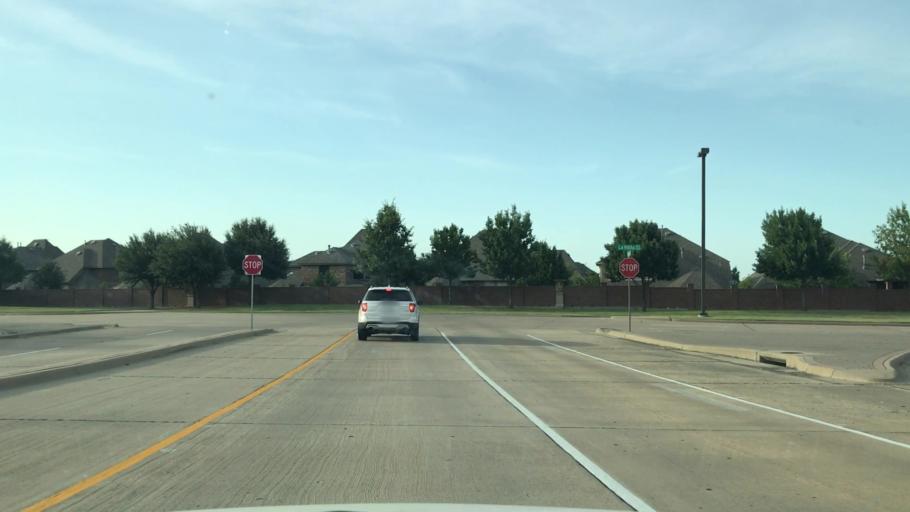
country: US
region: Texas
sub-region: Dallas County
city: Farmers Branch
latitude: 32.9020
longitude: -96.9453
